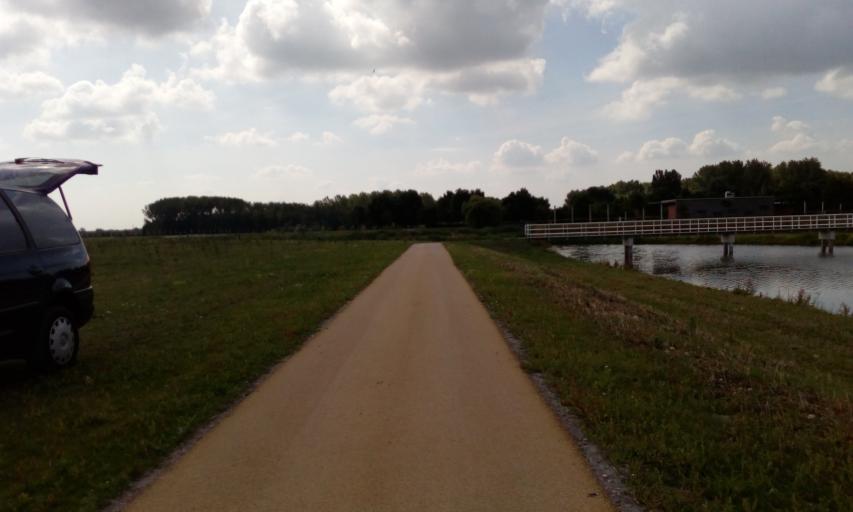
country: NL
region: South Holland
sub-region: Gemeente Pijnacker-Nootdorp
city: Pijnacker
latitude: 52.0374
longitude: 4.4127
